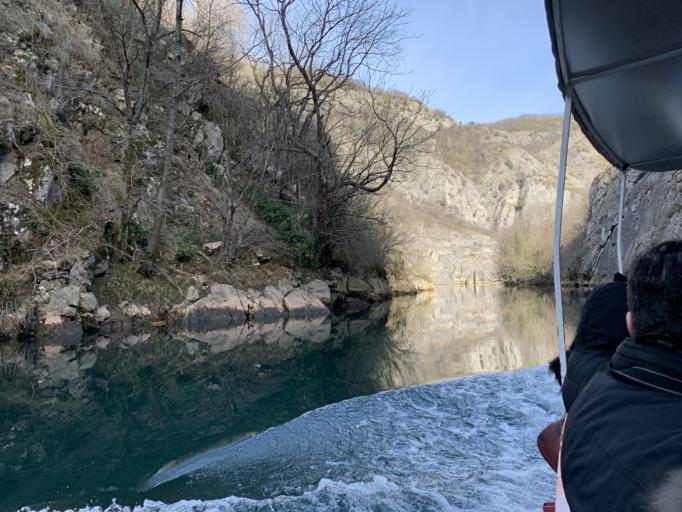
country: MK
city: Grchec
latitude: 41.9321
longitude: 21.2952
